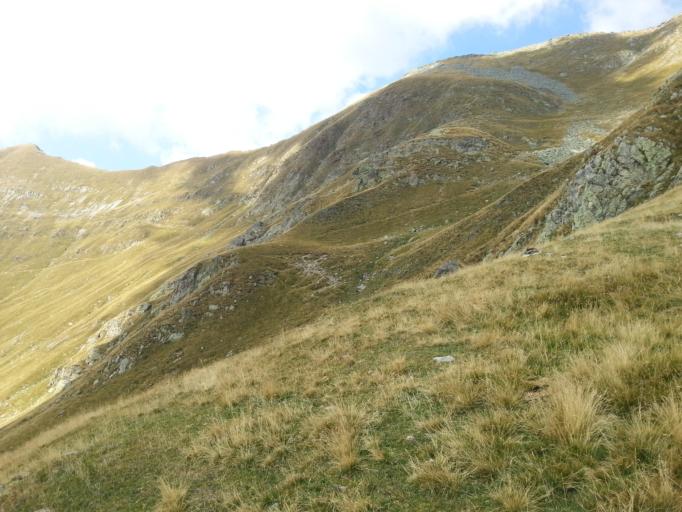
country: CH
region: Grisons
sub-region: Moesa District
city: Roveredo
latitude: 46.1659
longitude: 9.1713
